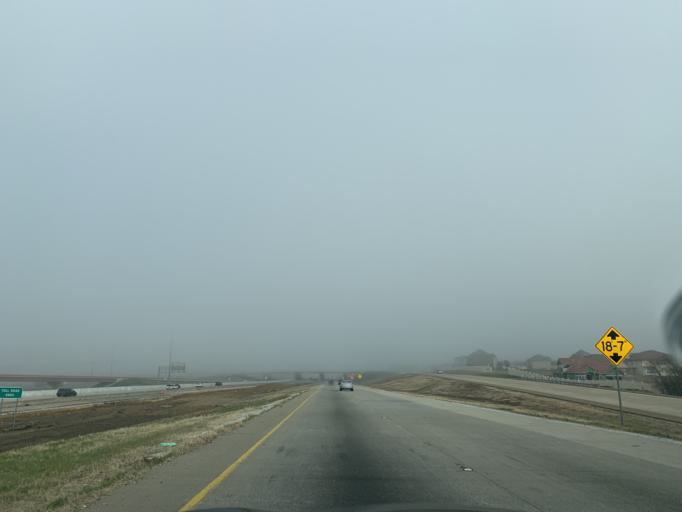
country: US
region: Texas
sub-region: Tarrant County
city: Euless
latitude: 32.8410
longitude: -97.0160
